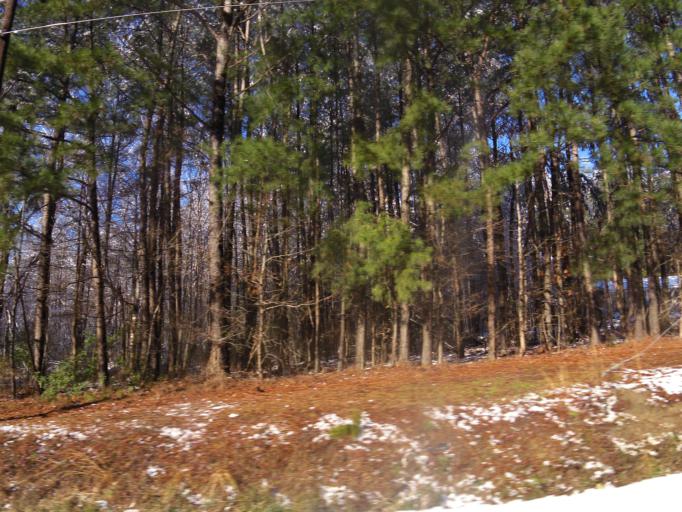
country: US
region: North Carolina
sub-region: Nash County
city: Sharpsburg
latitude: 35.8781
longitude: -77.8245
